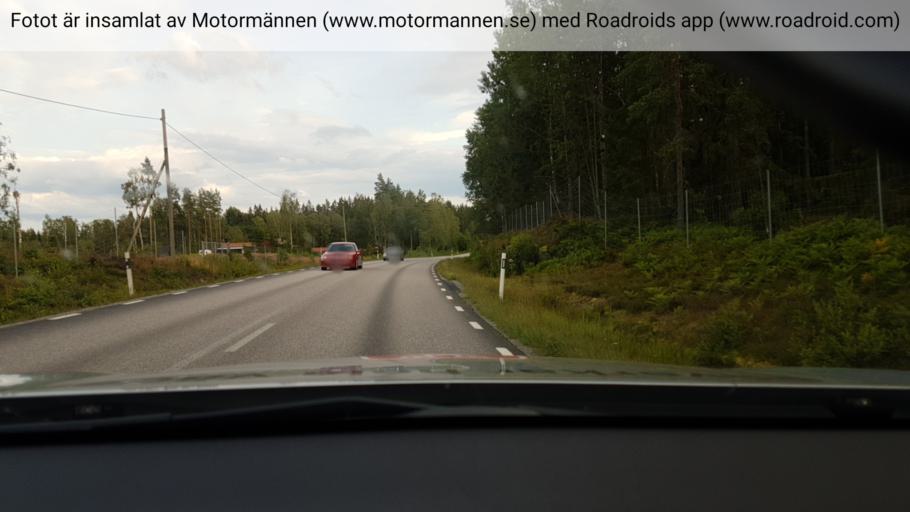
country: SE
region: Vaestra Goetaland
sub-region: Fargelanda Kommun
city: Faergelanda
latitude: 58.4742
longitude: 12.0134
